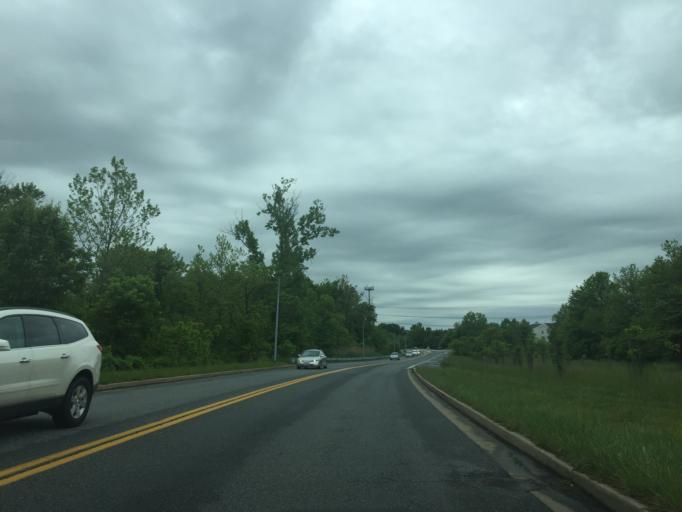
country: US
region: Maryland
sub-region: Baltimore County
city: Perry Hall
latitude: 39.3842
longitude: -76.4699
